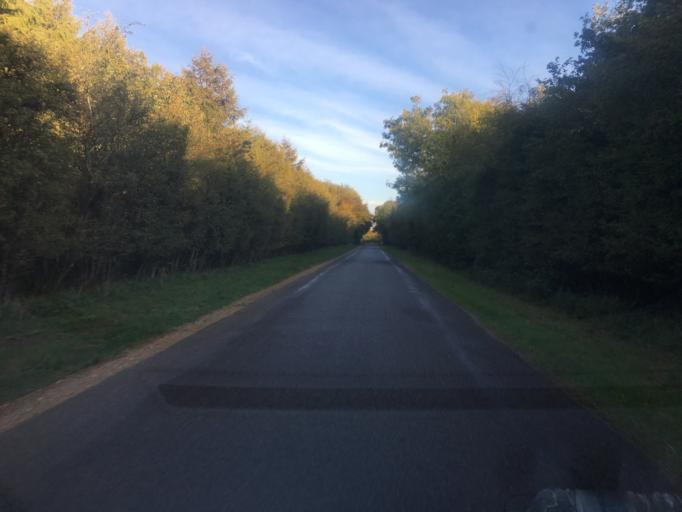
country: DE
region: Schleswig-Holstein
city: Ellhoft
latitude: 54.9142
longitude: 8.9866
